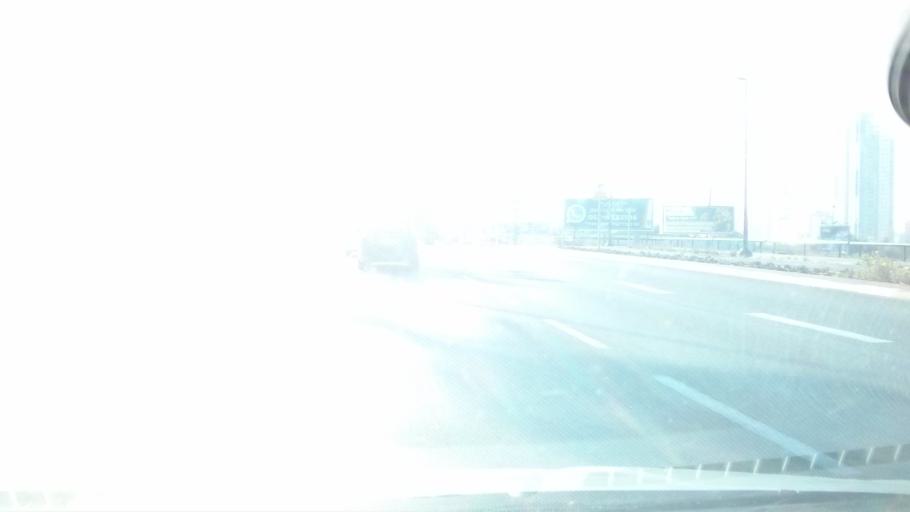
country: IL
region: Central District
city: Even Yehuda
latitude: 32.2845
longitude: 34.8444
